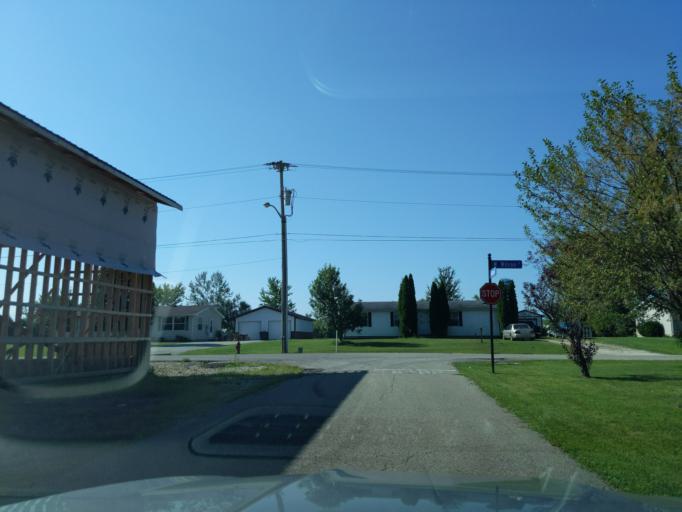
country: US
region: Indiana
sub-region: Ripley County
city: Osgood
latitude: 39.1248
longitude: -85.2934
